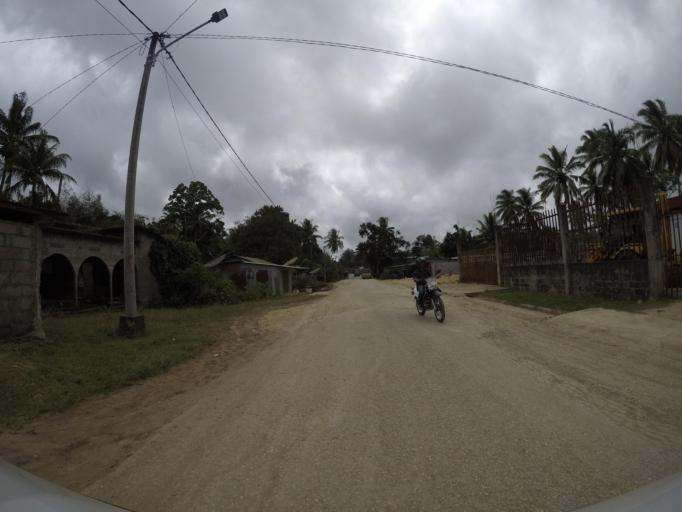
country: TL
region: Lautem
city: Lospalos
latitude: -8.5163
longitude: 127.0004
